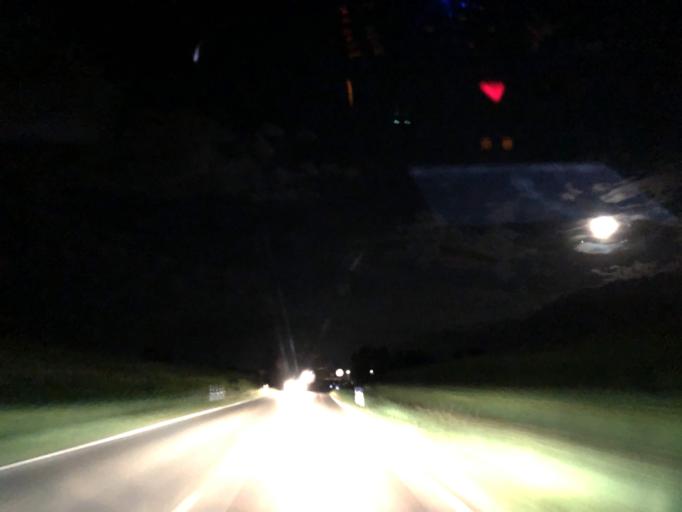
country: DE
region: Bavaria
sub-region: Upper Bavaria
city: Finsing
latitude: 48.2339
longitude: 11.8156
